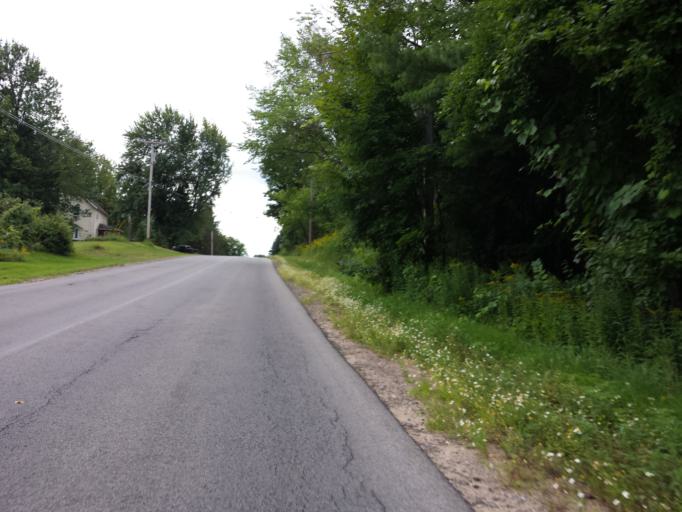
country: US
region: New York
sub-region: St. Lawrence County
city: Potsdam
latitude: 44.6996
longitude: -75.0120
